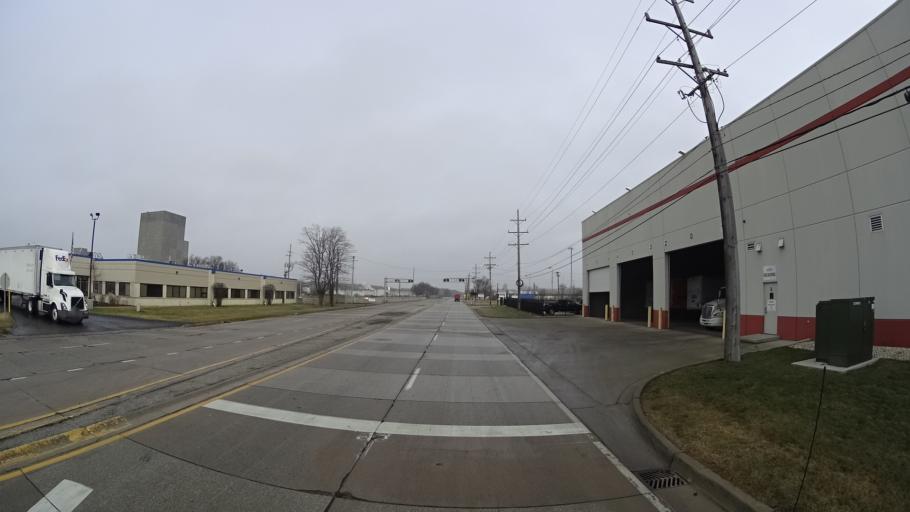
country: US
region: Illinois
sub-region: Cook County
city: Chicago Heights
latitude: 41.5214
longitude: -87.6163
